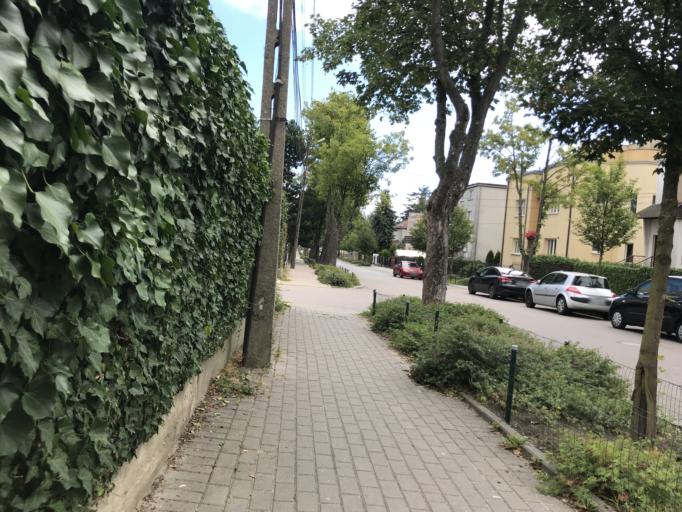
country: PL
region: Pomeranian Voivodeship
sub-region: Sopot
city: Sopot
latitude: 54.4767
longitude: 18.5577
